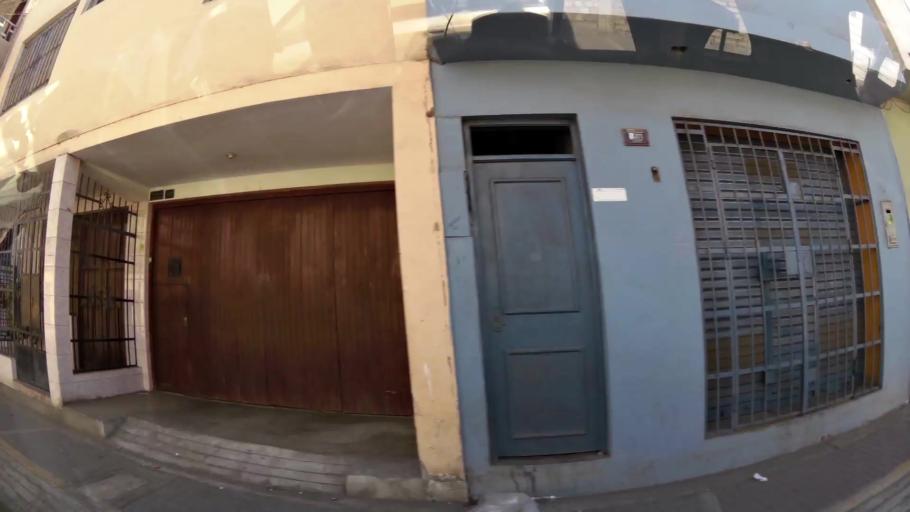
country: PE
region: Ica
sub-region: Provincia de Chincha
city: Chincha Alta
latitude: -13.4166
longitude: -76.1306
